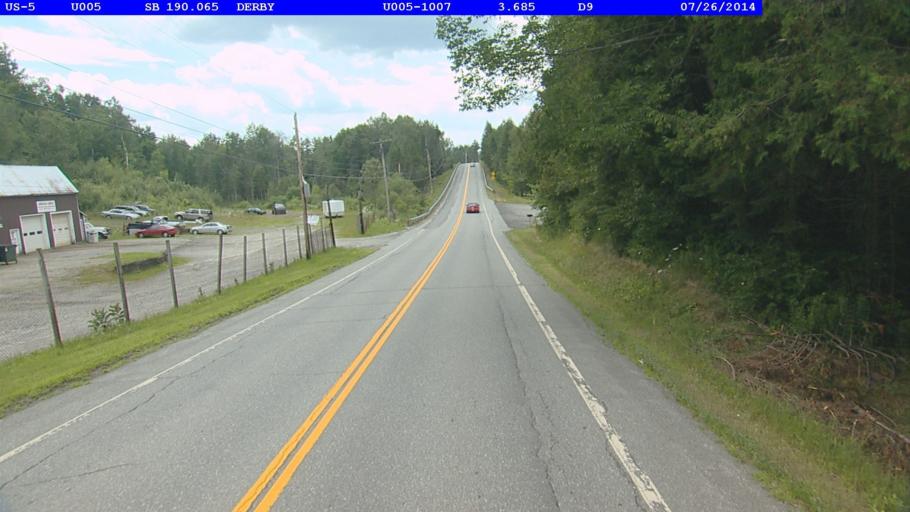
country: US
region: Vermont
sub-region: Orleans County
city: Newport
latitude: 44.9762
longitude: -72.1152
